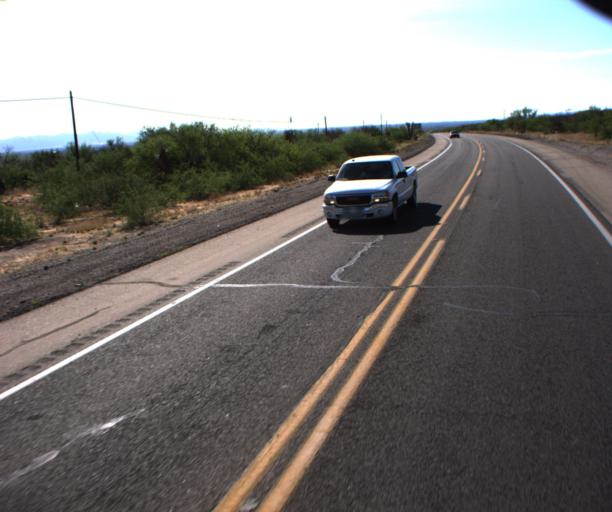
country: US
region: Arizona
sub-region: Cochise County
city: Benson
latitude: 31.9324
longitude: -110.2838
